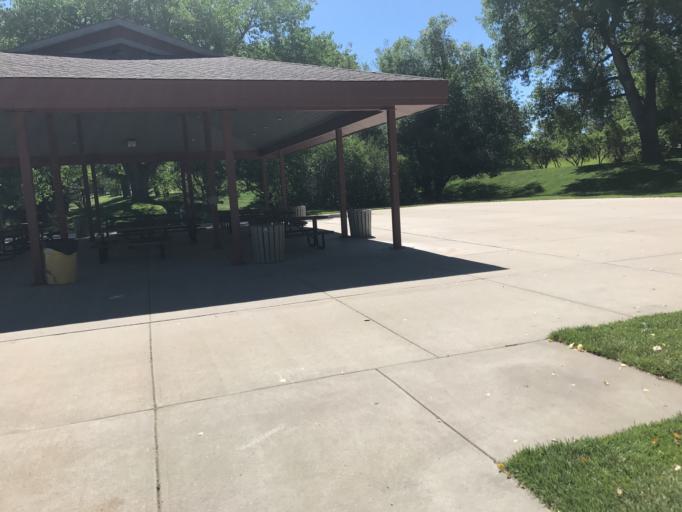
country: US
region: Colorado
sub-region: Broomfield County
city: Broomfield
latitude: 39.9209
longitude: -105.1083
